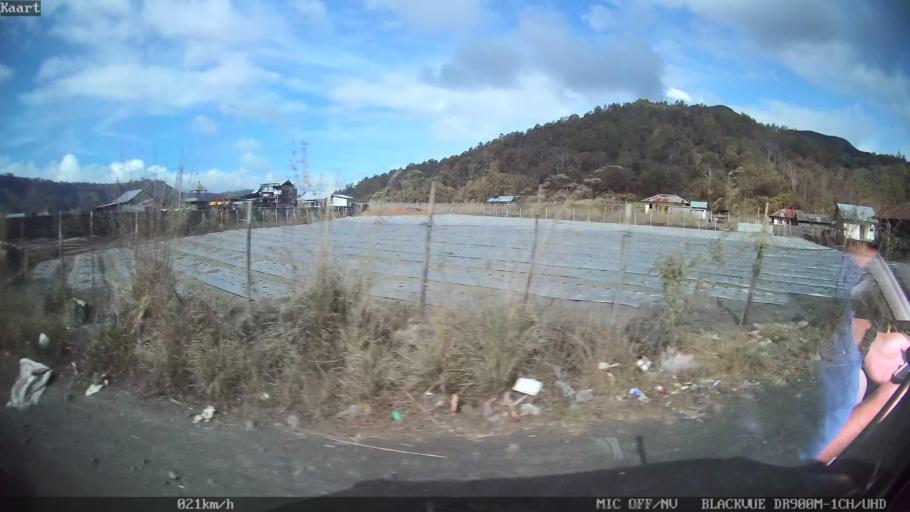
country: ID
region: Bali
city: Banjar Kedisan
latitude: -8.2269
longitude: 115.3594
